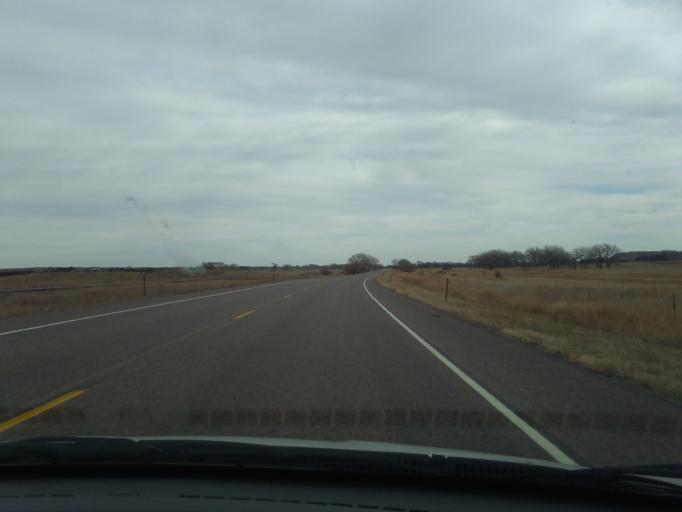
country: US
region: Colorado
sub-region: Yuma County
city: Wray
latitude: 40.0859
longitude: -102.1309
